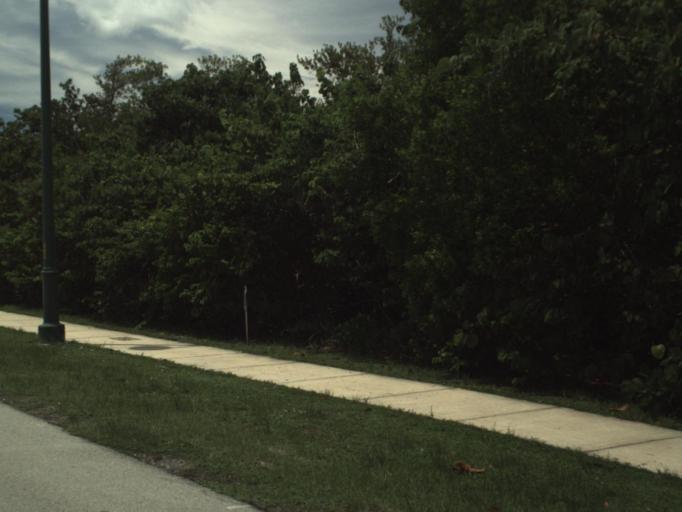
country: US
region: Florida
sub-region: Palm Beach County
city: Palm Beach Shores
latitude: 26.8065
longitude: -80.0353
